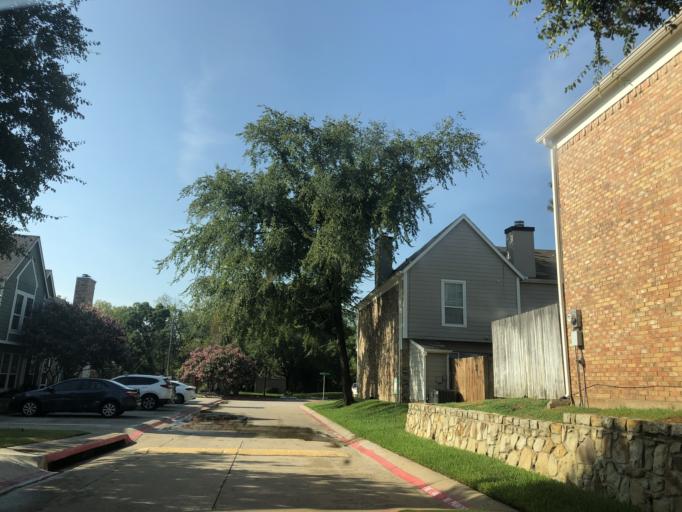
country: US
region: Texas
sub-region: Tarrant County
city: Euless
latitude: 32.8682
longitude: -97.0807
